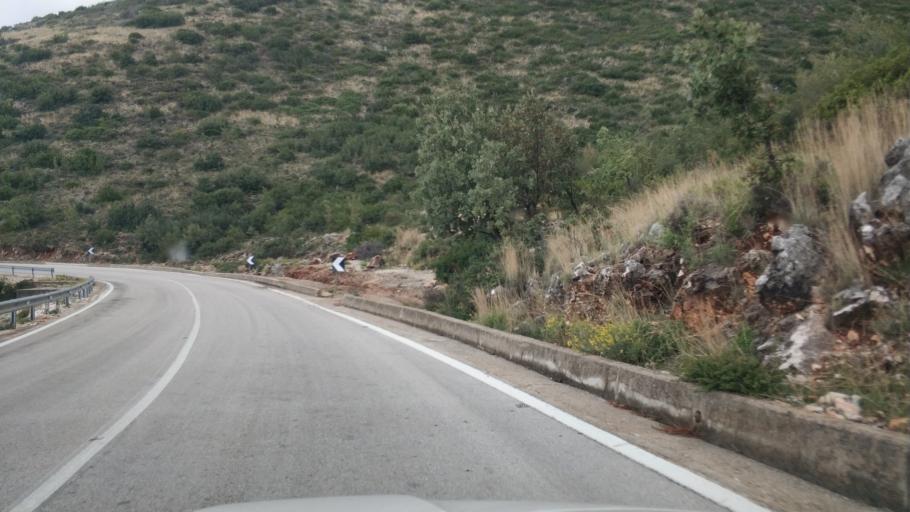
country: AL
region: Vlore
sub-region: Rrethi i Vlores
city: Vranisht
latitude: 40.1453
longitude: 19.6604
